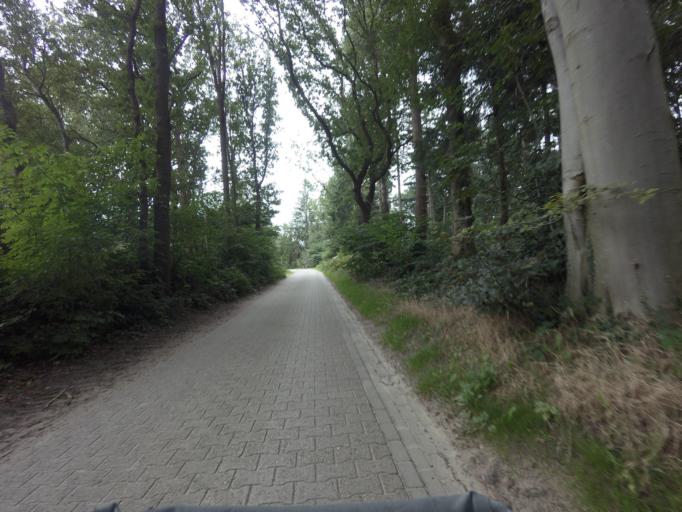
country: NL
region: Overijssel
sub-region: Gemeente Steenwijkerland
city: Tuk
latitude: 52.8183
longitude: 6.1093
